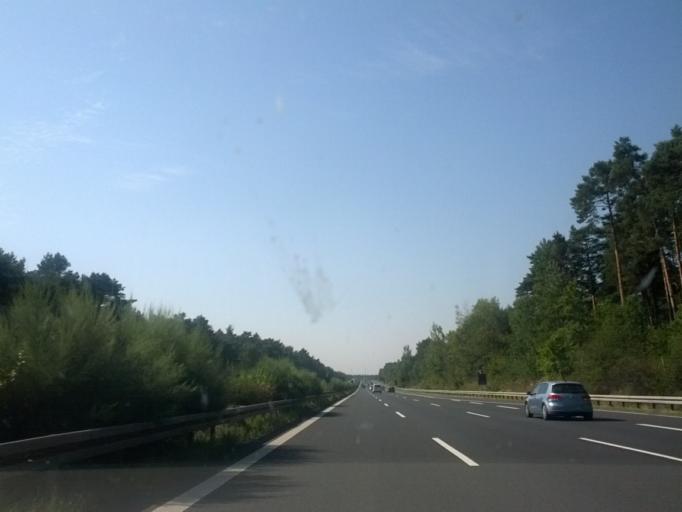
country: DE
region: Brandenburg
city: Borkheide
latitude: 52.2116
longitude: 12.8952
